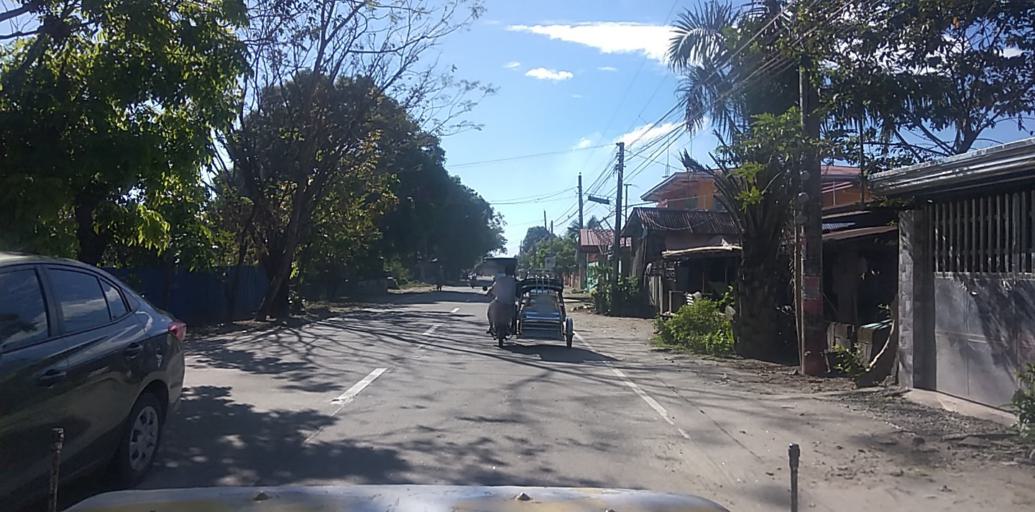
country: PH
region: Central Luzon
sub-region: Province of Pampanga
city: San Patricio
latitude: 15.0844
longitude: 120.7155
